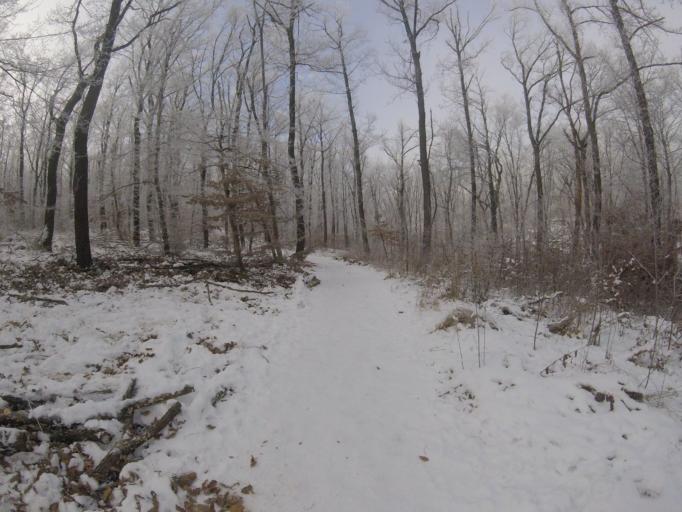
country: HU
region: Pest
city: Pilisszentivan
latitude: 47.5888
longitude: 18.9064
